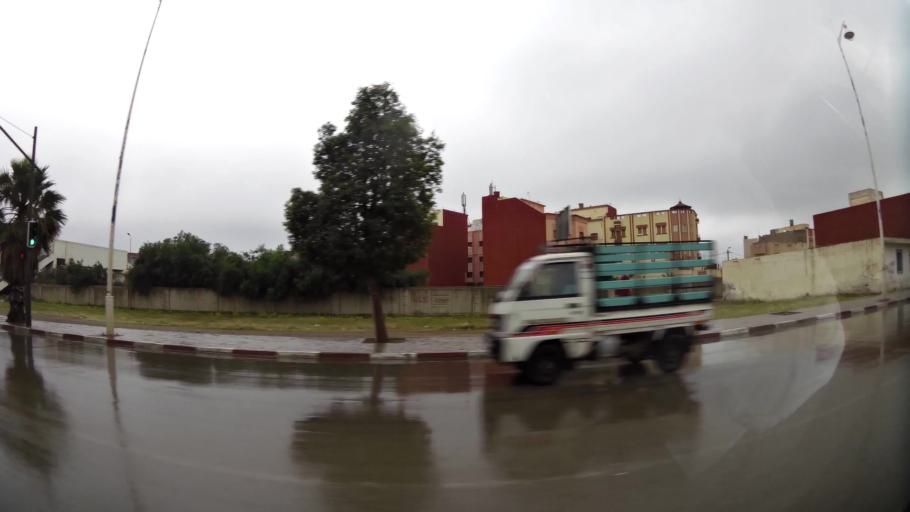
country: MA
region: Oriental
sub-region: Nador
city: Nador
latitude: 35.1628
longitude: -2.9619
